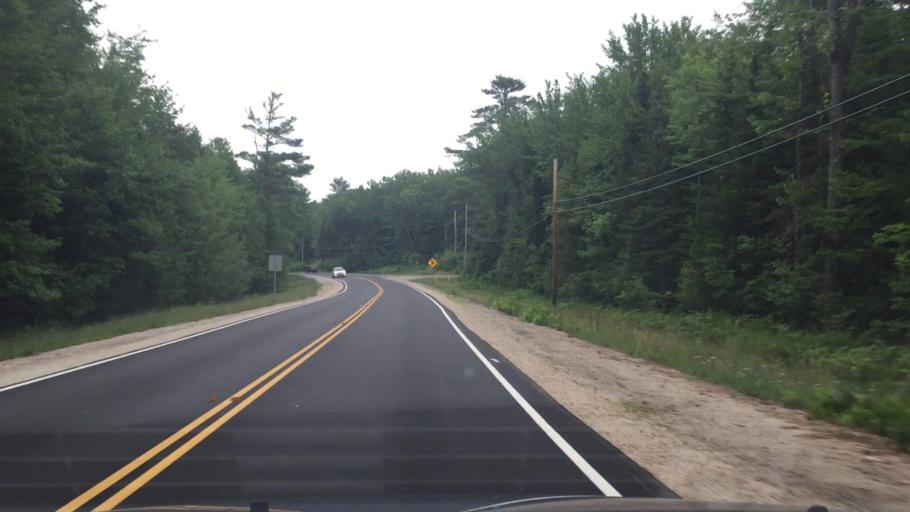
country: US
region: New Hampshire
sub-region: Carroll County
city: Freedom
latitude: 43.8076
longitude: -71.0647
